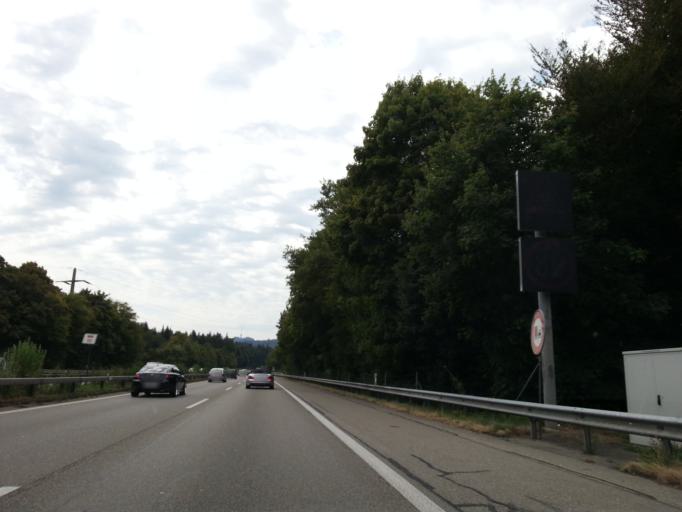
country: CH
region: Bern
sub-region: Emmental District
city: Hindelbank
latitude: 47.0403
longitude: 7.5286
